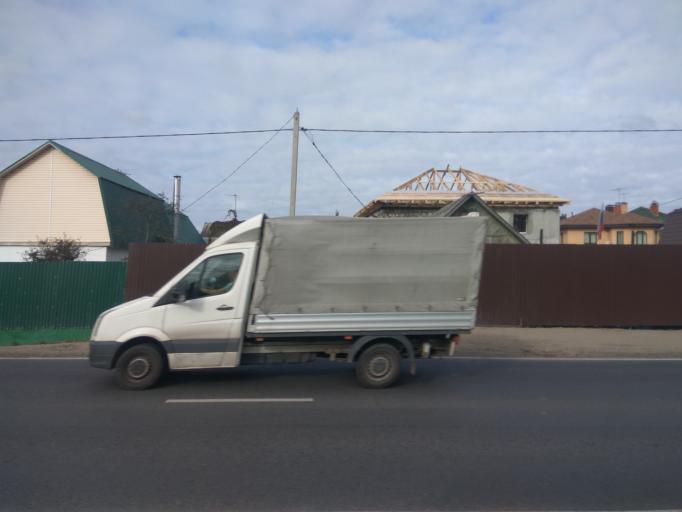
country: RU
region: Moskovskaya
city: Medvezh'i Ozera
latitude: 55.8670
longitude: 37.9915
